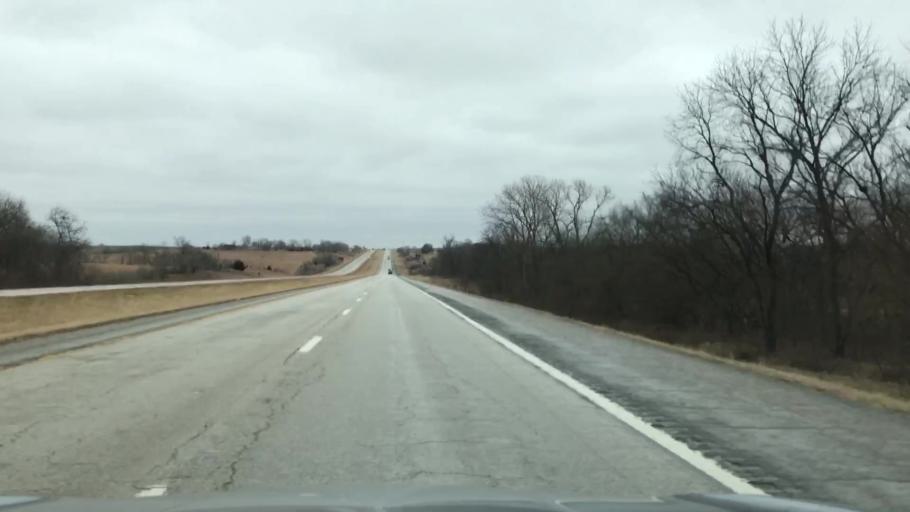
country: US
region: Missouri
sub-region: Caldwell County
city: Hamilton
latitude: 39.7500
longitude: -94.1042
